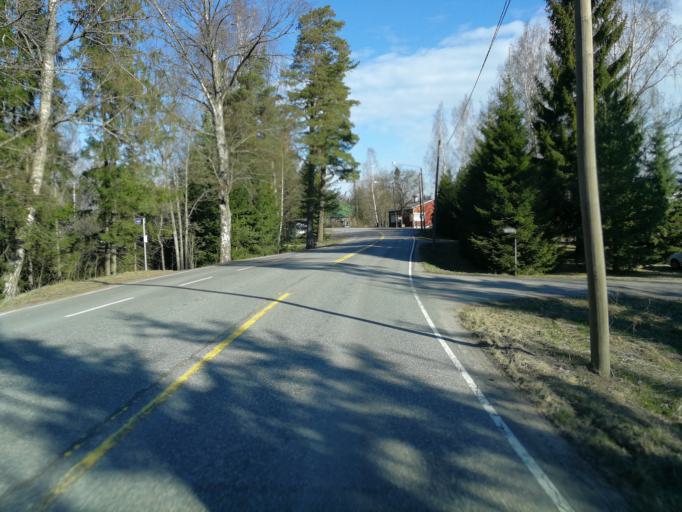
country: FI
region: Uusimaa
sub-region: Helsinki
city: Kirkkonummi
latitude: 60.2135
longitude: 24.4846
